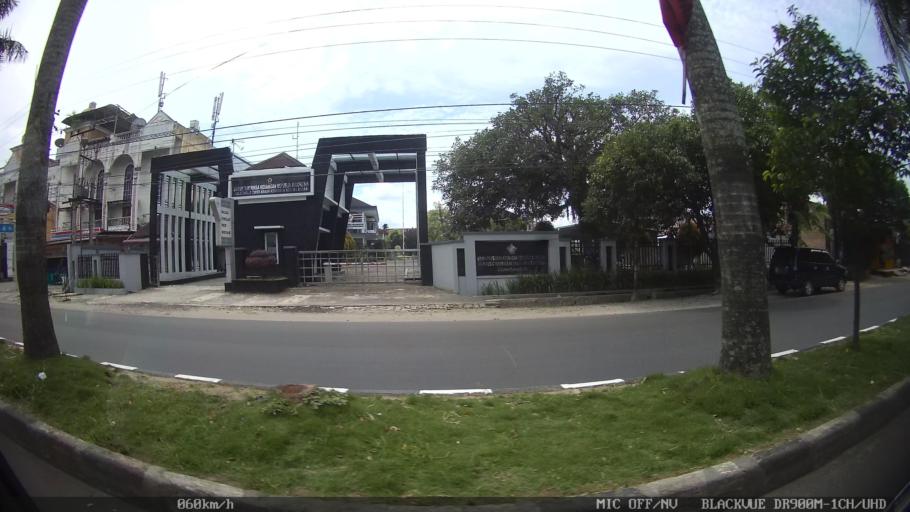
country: ID
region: North Sumatra
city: Sunggal
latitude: 3.5225
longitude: 98.6248
